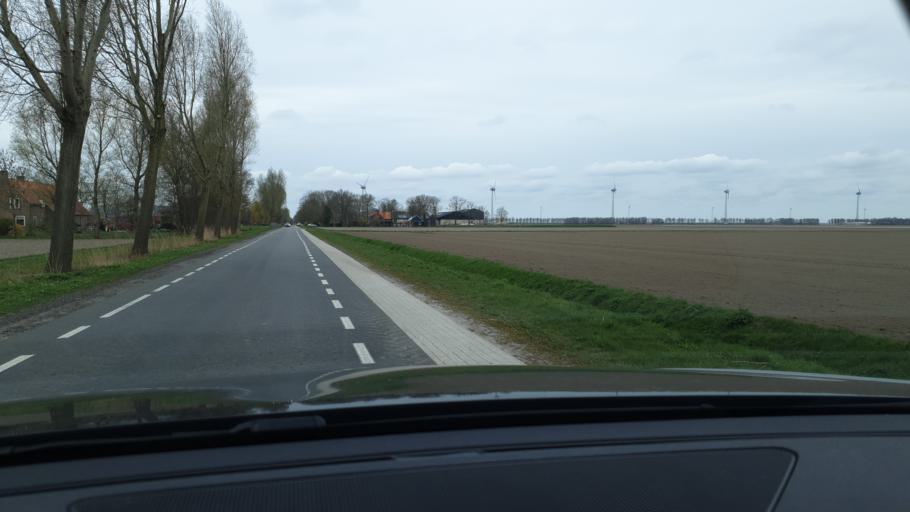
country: NL
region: Friesland
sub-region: Gemeente Lemsterland
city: Lemmer
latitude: 52.7706
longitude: 5.6501
